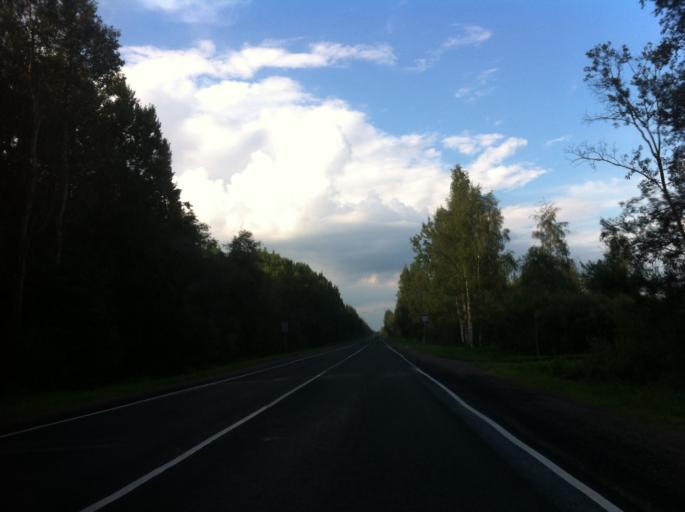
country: RU
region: Leningrad
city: Luga
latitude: 58.4923
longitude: 29.7824
